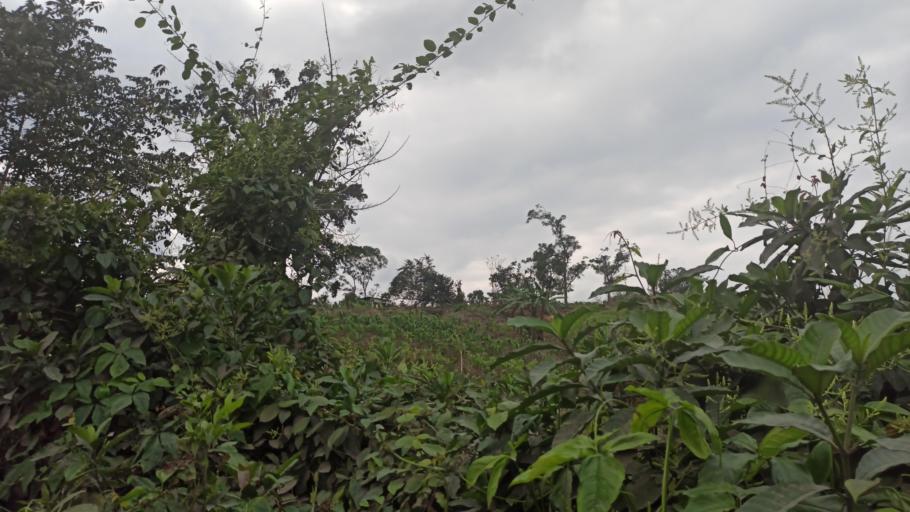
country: MX
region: Veracruz
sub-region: Papantla
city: El Chote
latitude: 20.3856
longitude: -97.4217
